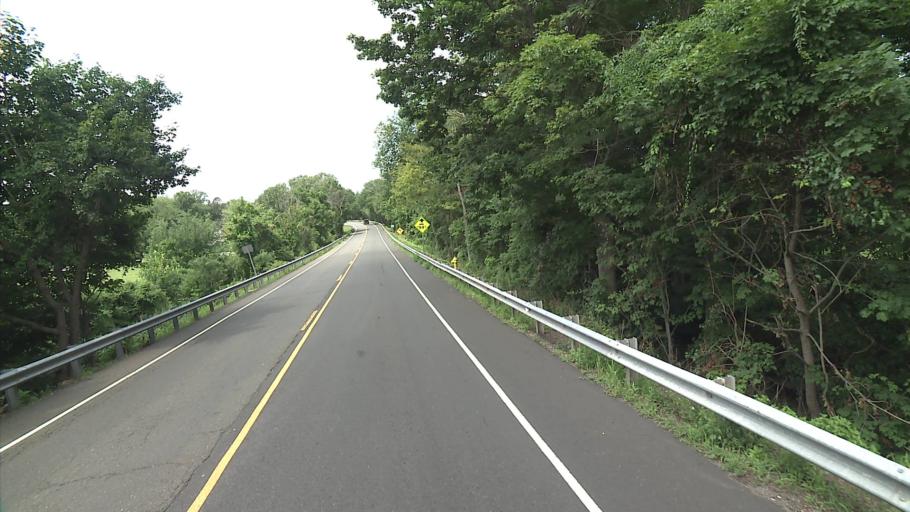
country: US
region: Connecticut
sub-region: New Haven County
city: North Haven
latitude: 41.3806
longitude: -72.8091
